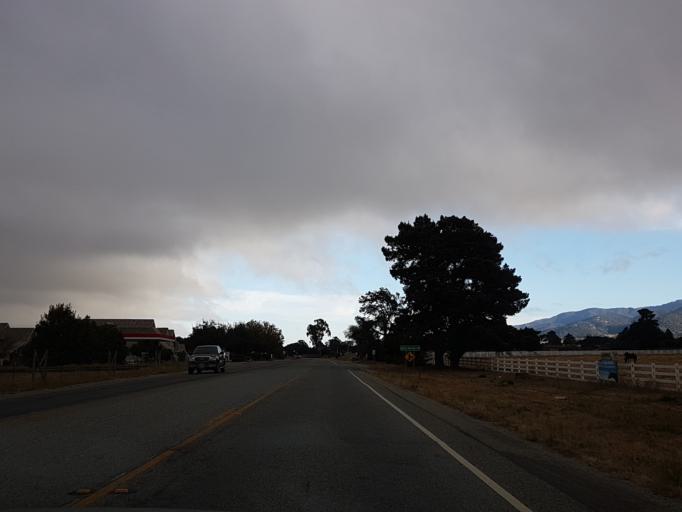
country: US
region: California
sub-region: Monterey County
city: Salinas
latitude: 36.6027
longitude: -121.6356
